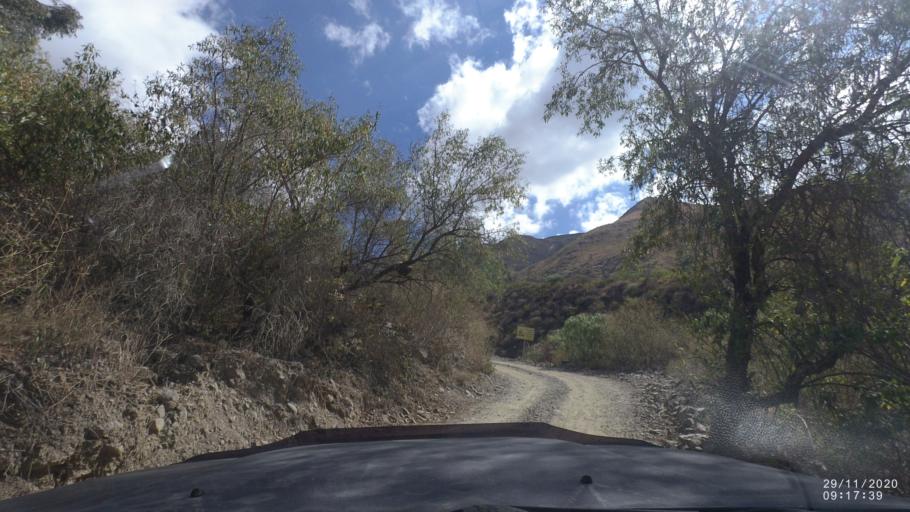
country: BO
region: Cochabamba
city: Cochabamba
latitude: -17.3235
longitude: -66.1837
